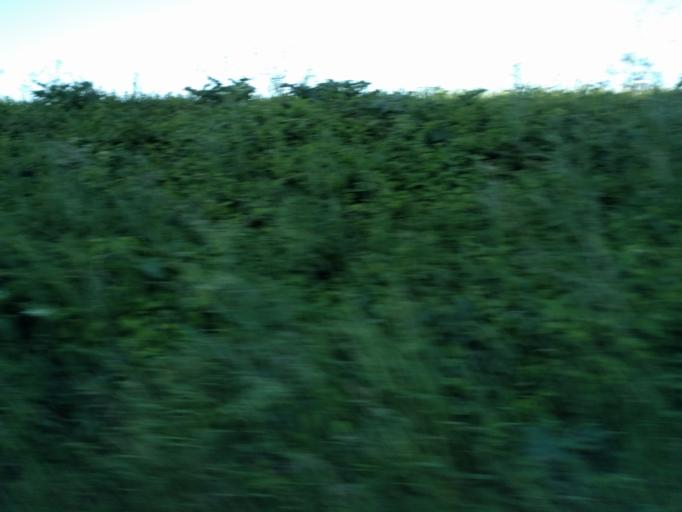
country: DK
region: South Denmark
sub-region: Kerteminde Kommune
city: Kerteminde
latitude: 55.5686
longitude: 10.6468
